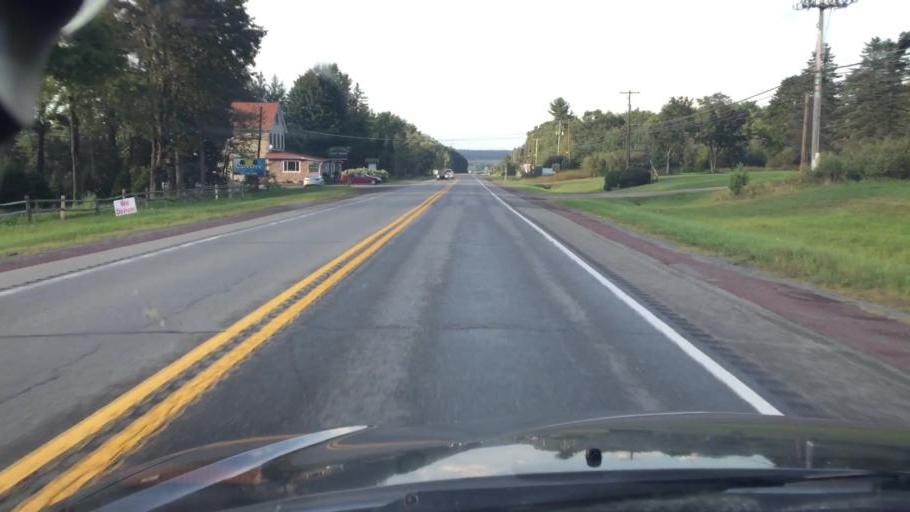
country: US
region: Pennsylvania
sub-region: Carbon County
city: Towamensing Trails
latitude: 40.9475
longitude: -75.6528
